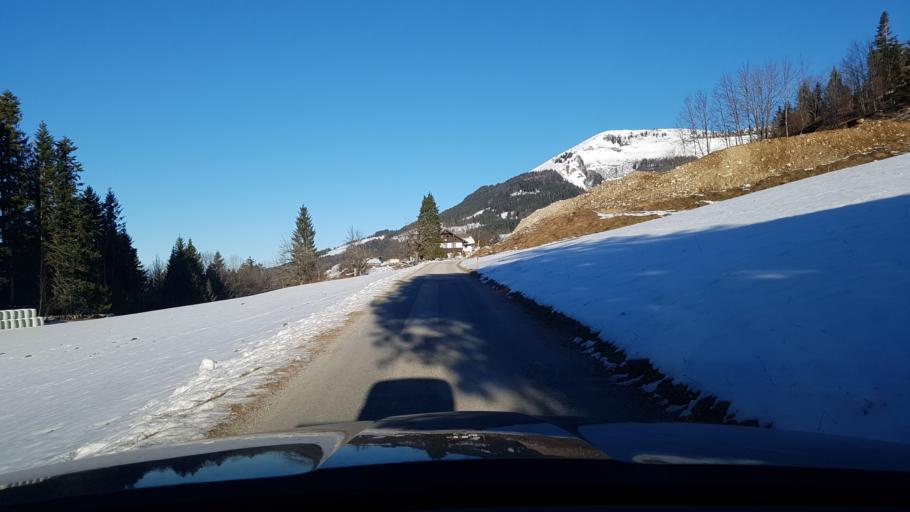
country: AT
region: Salzburg
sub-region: Politischer Bezirk Hallein
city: Scheffau am Tennengebirge
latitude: 47.6484
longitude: 13.2276
